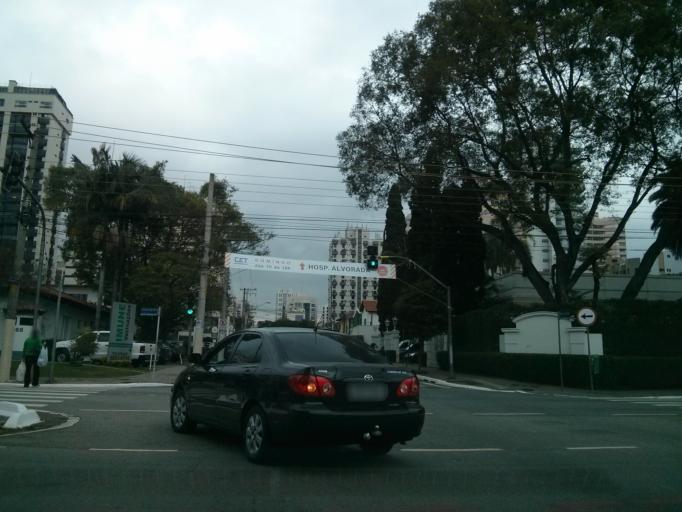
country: BR
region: Sao Paulo
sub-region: Sao Paulo
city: Sao Paulo
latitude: -23.6021
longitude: -46.6562
